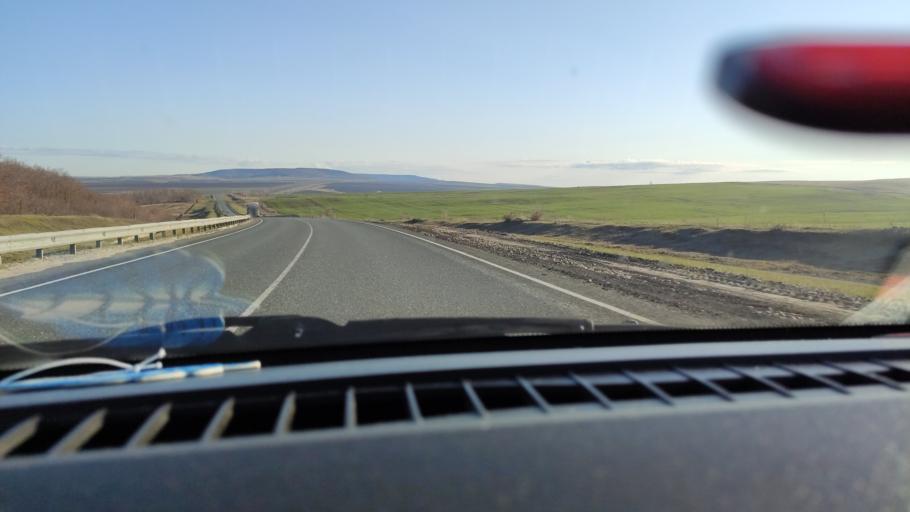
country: RU
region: Saratov
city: Alekseyevka
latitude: 52.2242
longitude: 47.9008
